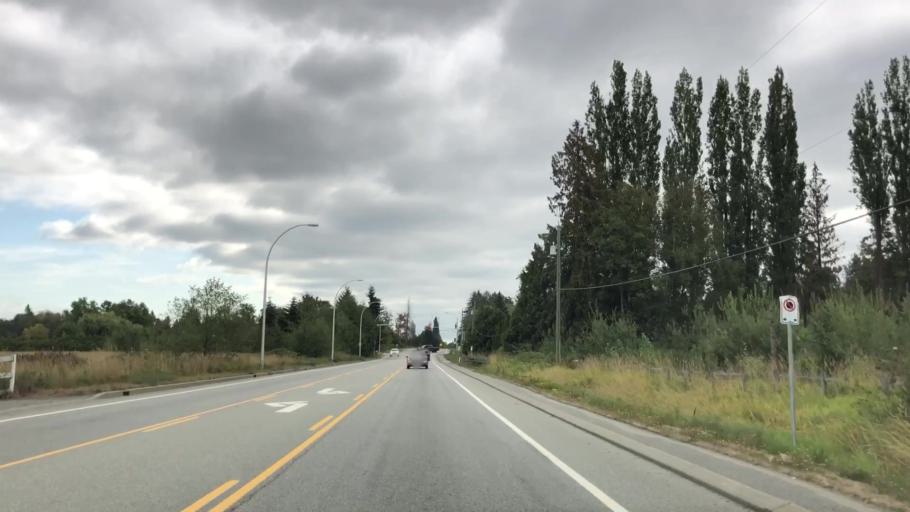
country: CA
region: British Columbia
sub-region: Greater Vancouver Regional District
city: White Rock
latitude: 49.0603
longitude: -122.7598
